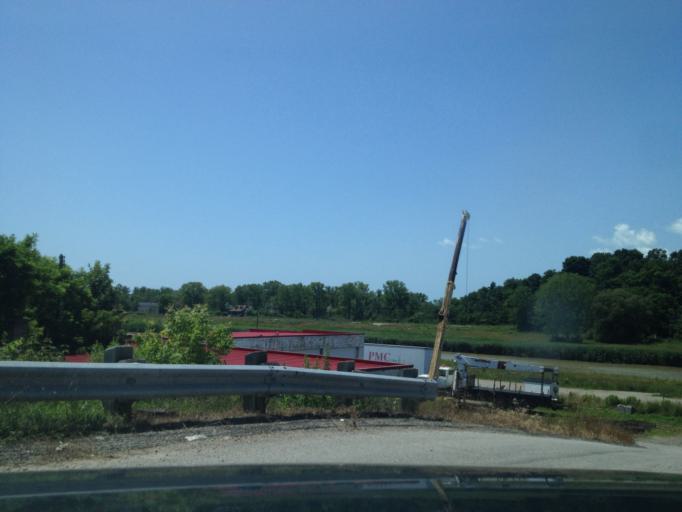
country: CA
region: Ontario
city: Aylmer
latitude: 42.6457
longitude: -80.8069
